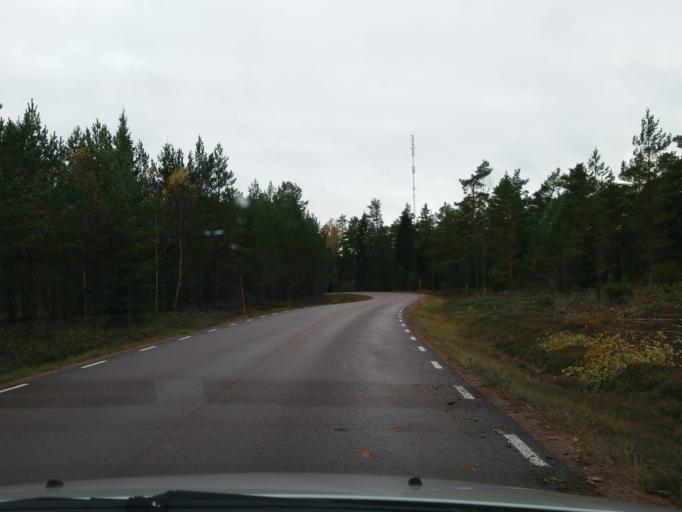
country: AX
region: Alands landsbygd
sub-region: Lemland
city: Lemland
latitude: 60.0634
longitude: 20.1627
